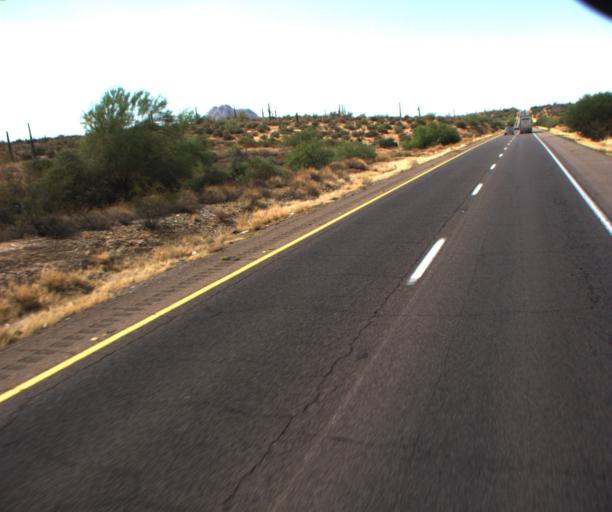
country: US
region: Arizona
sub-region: Maricopa County
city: New River
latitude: 33.9452
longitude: -112.1405
